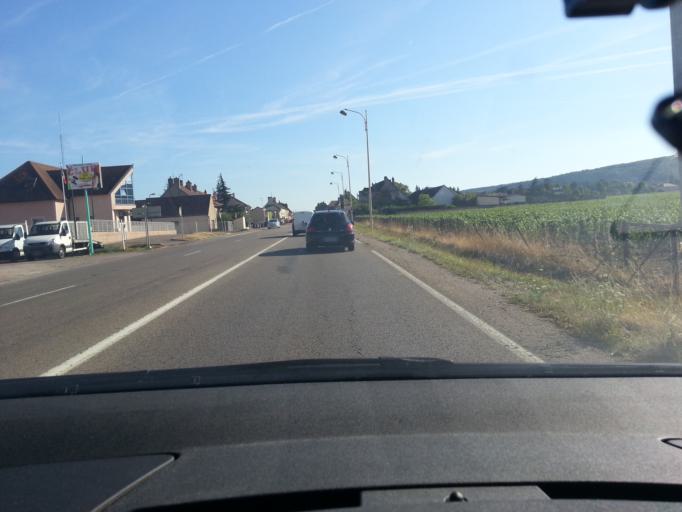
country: FR
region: Bourgogne
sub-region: Departement de la Cote-d'Or
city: Gevrey-Chambertin
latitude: 47.2321
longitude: 4.9822
